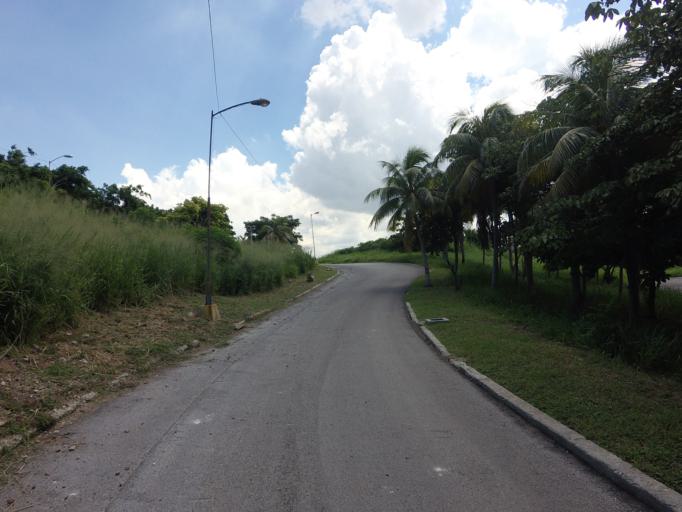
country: CU
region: La Habana
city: Centro Habana
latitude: 23.1498
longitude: -82.3542
